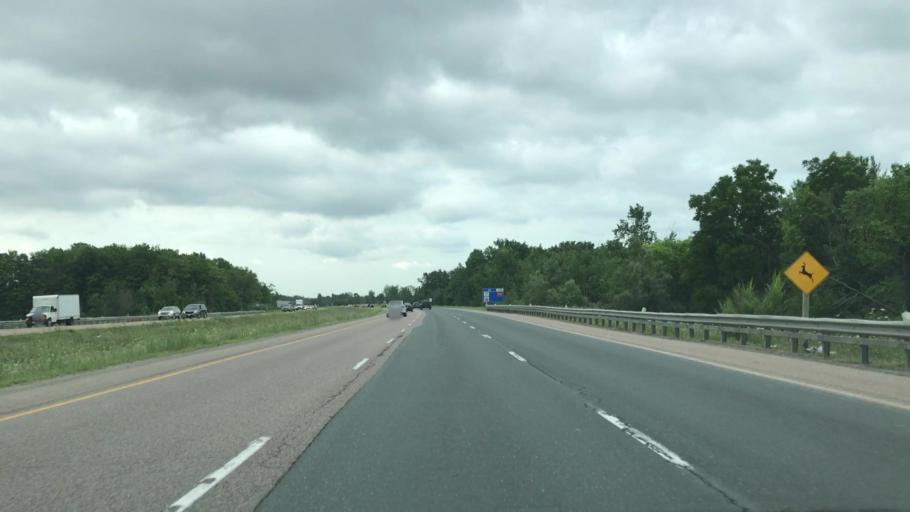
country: CA
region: Ontario
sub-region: York
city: Richmond Hill
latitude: 43.9306
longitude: -79.3904
